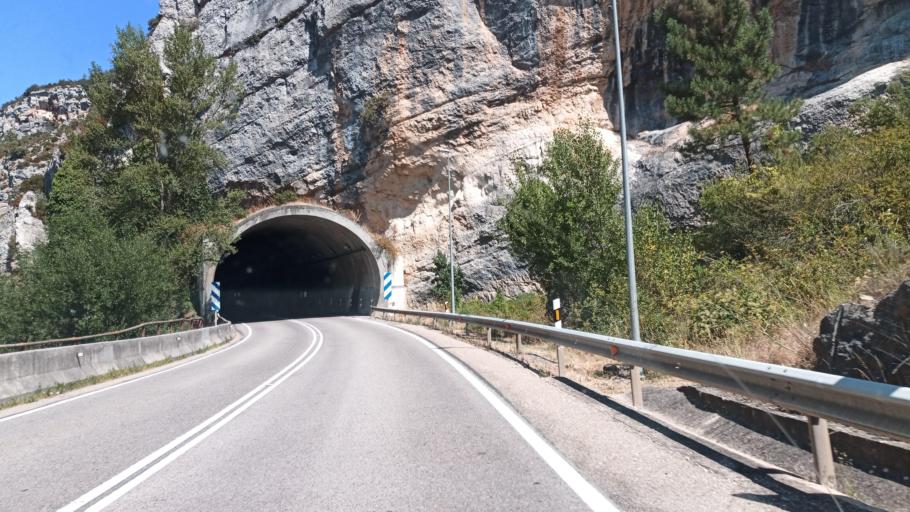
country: ES
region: Castille and Leon
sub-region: Provincia de Burgos
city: Ona
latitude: 42.7443
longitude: -3.4083
